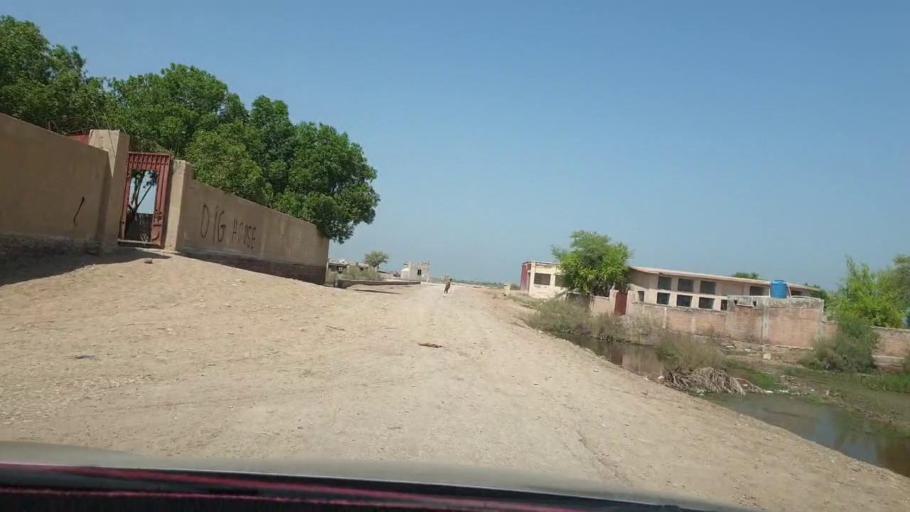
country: PK
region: Sindh
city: Warah
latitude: 27.5787
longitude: 67.7581
